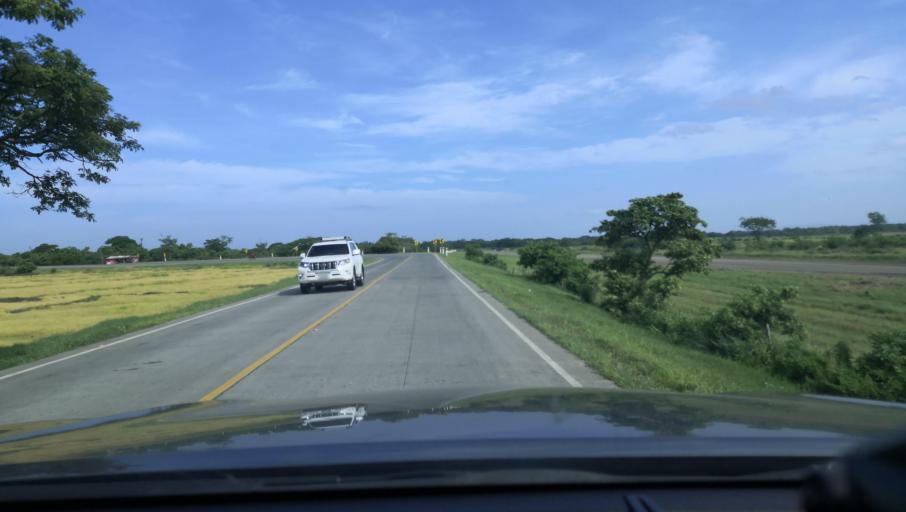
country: NI
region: Masaya
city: Tisma
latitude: 12.1542
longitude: -85.8427
